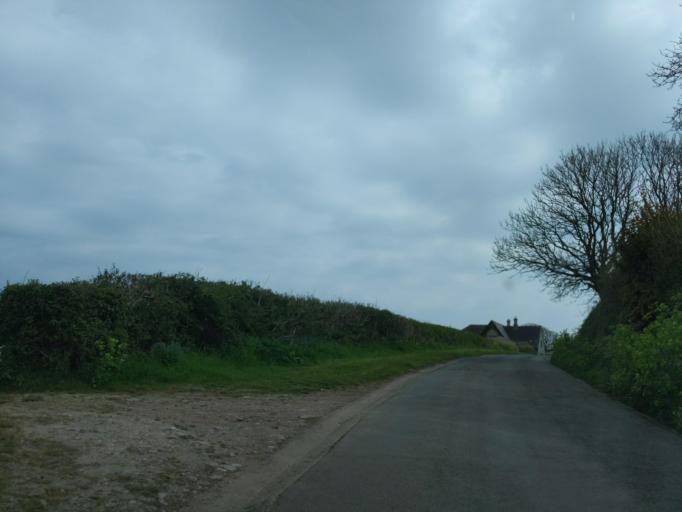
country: GB
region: England
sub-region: Devon
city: Dartmouth
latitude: 50.3636
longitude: -3.5507
